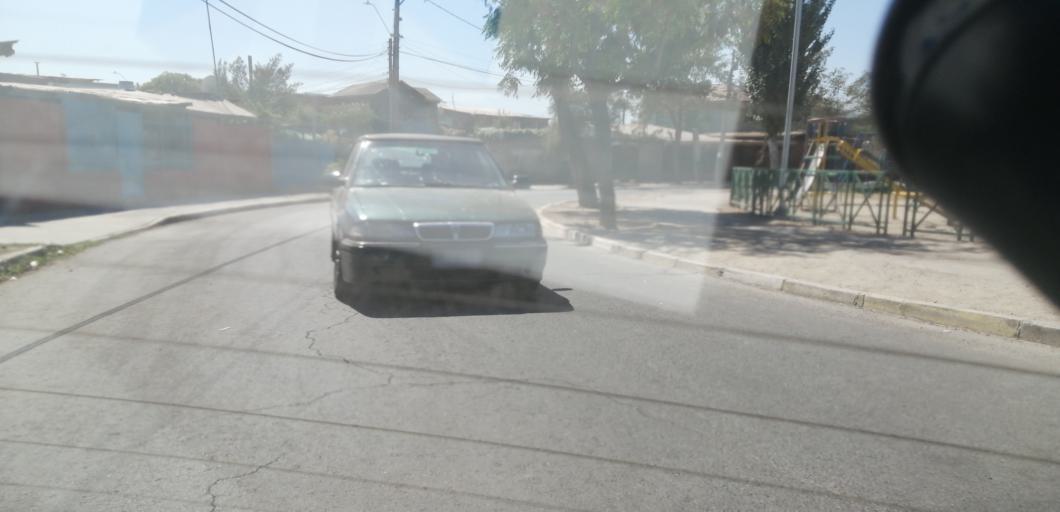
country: CL
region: Santiago Metropolitan
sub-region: Provincia de Santiago
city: Lo Prado
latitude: -33.4379
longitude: -70.7663
